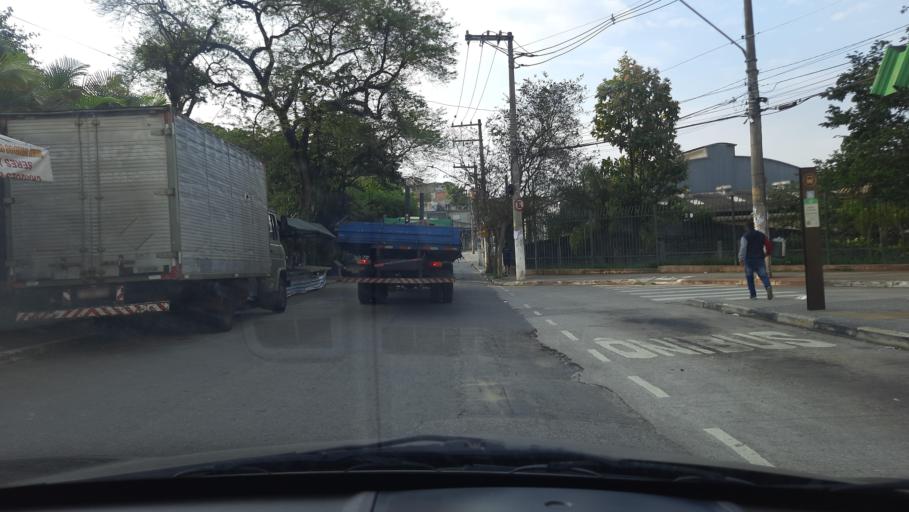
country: BR
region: Sao Paulo
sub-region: Caieiras
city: Caieiras
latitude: -23.4387
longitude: -46.7481
